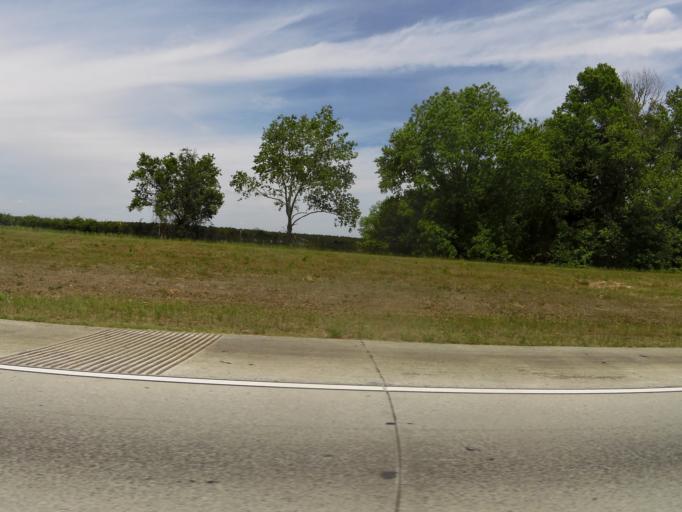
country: US
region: Georgia
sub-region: Candler County
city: Metter
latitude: 32.3568
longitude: -81.9908
